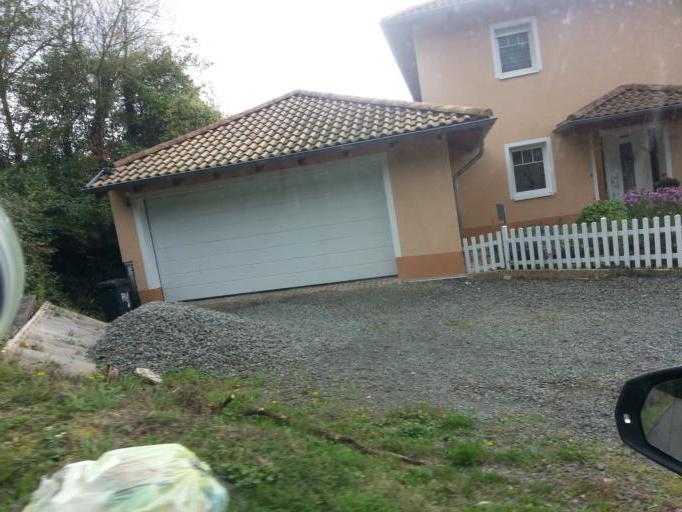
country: DE
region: Rheinland-Pfalz
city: Hahnweiler
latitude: 49.5324
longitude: 7.2197
